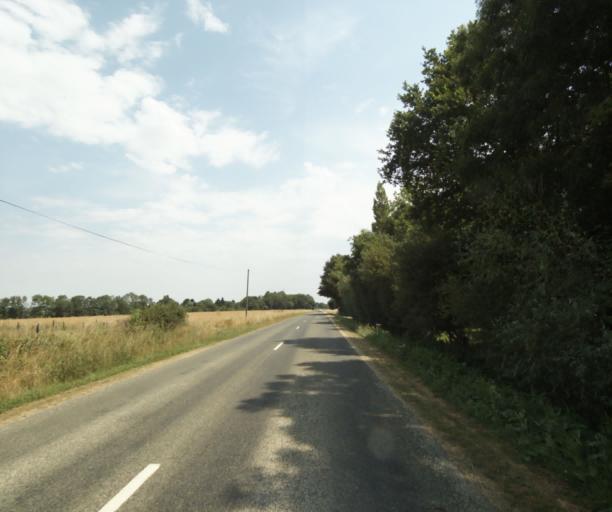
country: FR
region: Centre
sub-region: Departement d'Eure-et-Loir
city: Unverre
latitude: 48.1830
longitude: 1.0394
